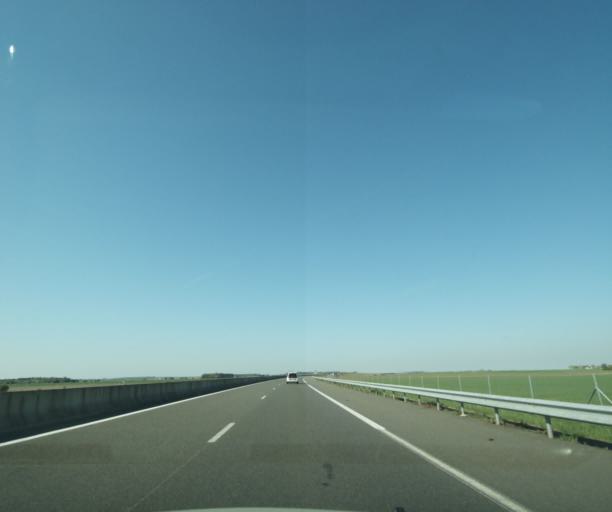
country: FR
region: Centre
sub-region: Departement du Loiret
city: Chilleurs-aux-Bois
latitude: 48.0985
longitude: 2.1154
